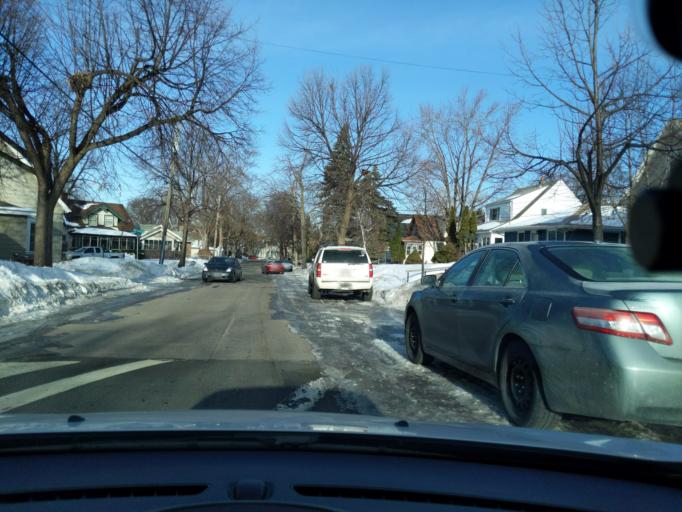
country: US
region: Minnesota
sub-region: Ramsey County
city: Lauderdale
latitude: 44.9864
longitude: -93.2196
